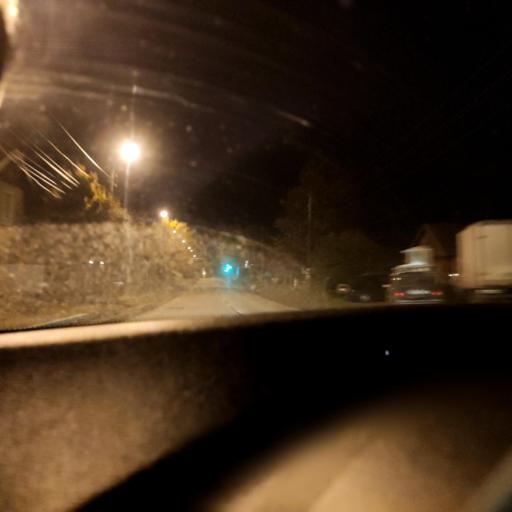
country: RU
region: Samara
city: Samara
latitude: 53.1777
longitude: 50.1691
